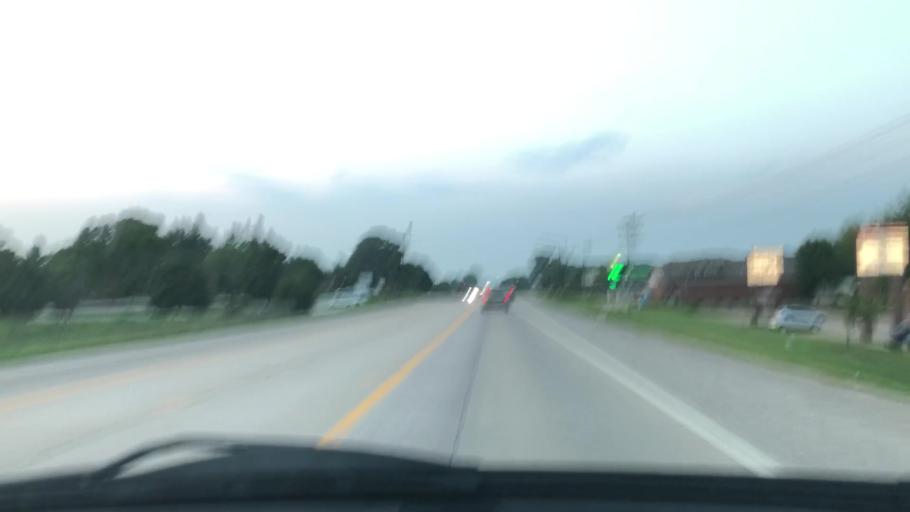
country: US
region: Iowa
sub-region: Johnson County
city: North Liberty
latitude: 41.7329
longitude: -91.6076
